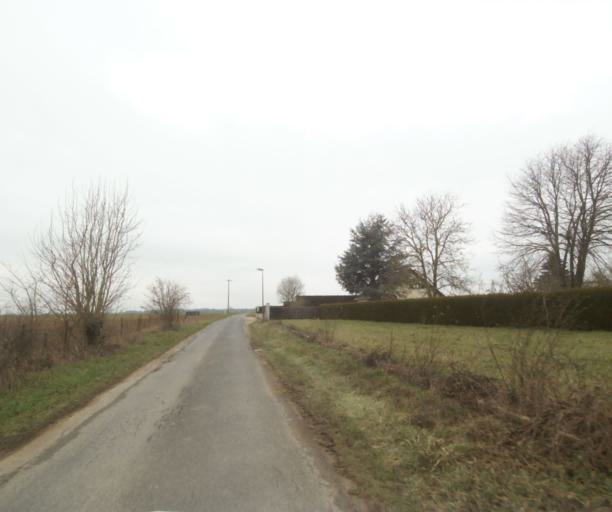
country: FR
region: Champagne-Ardenne
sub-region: Departement de la Haute-Marne
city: Villiers-en-Lieu
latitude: 48.6335
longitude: 4.8326
